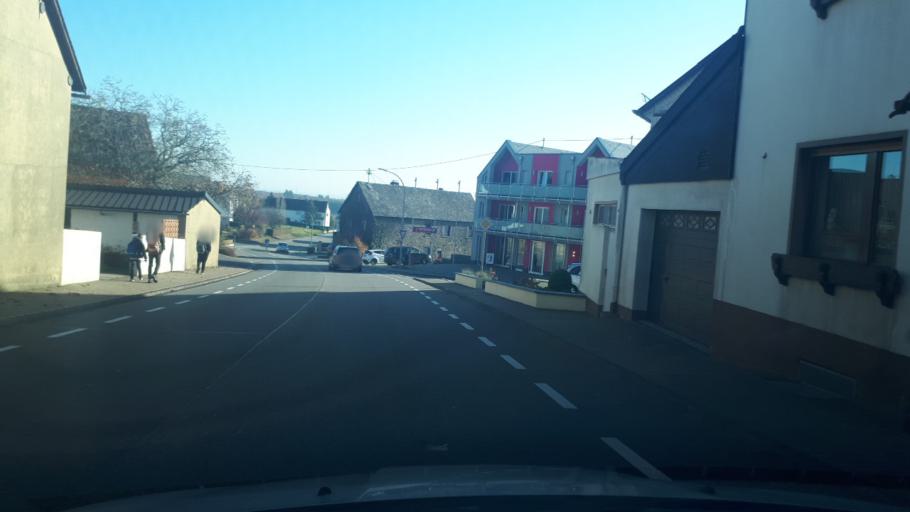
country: DE
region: Rheinland-Pfalz
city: Buchel
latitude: 50.1725
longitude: 7.0834
